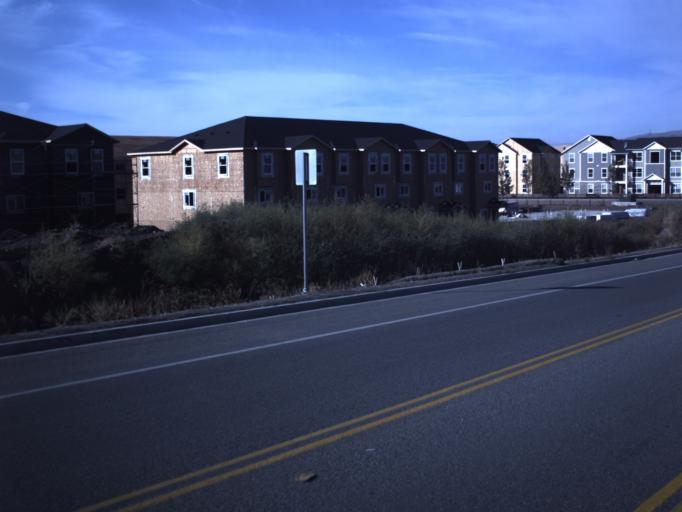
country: US
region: Utah
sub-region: Utah County
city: Lindon
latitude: 40.3101
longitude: -111.7521
